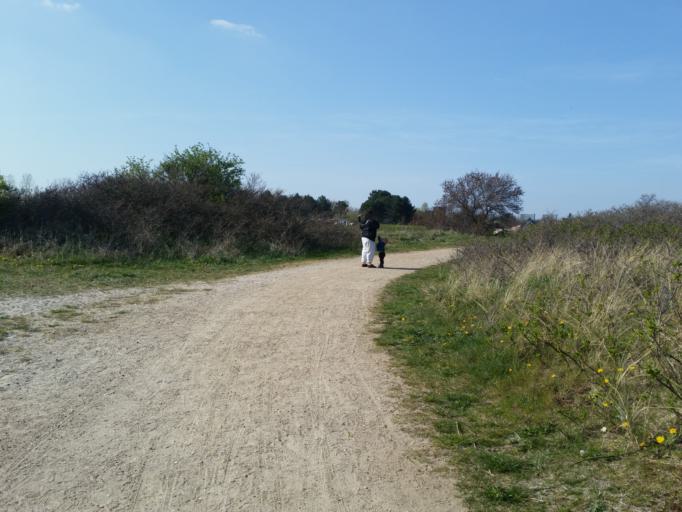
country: DK
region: Capital Region
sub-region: Brondby Kommune
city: Brondbyvester
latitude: 55.6126
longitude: 12.4005
